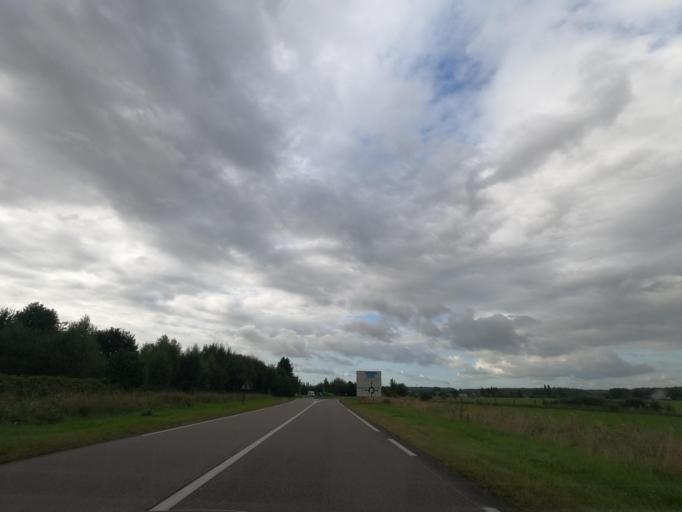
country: FR
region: Haute-Normandie
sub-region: Departement de l'Eure
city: Bourgtheroulde-Infreville
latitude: 49.3009
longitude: 0.8837
